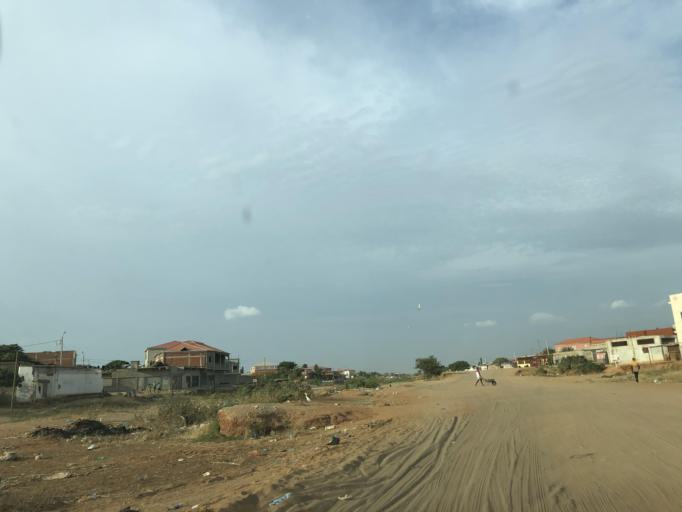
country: AO
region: Luanda
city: Luanda
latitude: -8.9241
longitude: 13.3061
